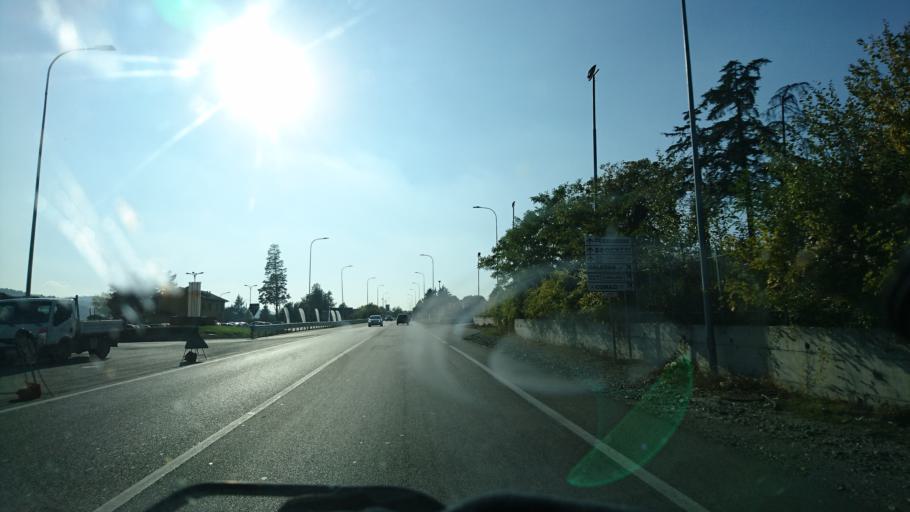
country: IT
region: Piedmont
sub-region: Provincia di Alessandria
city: Visone
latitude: 44.6816
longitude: 8.5022
